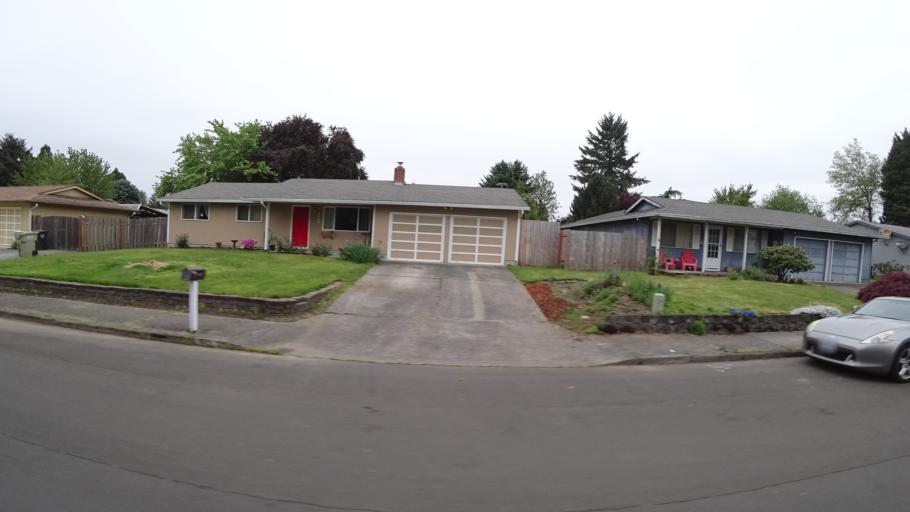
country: US
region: Oregon
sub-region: Washington County
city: Aloha
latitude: 45.5081
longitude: -122.8773
